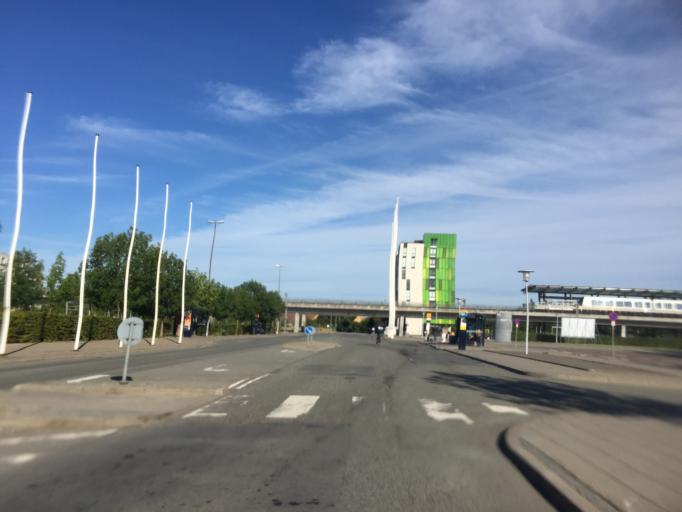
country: DK
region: Capital Region
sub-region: Tarnby Kommune
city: Tarnby
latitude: 55.6389
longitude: 12.5811
